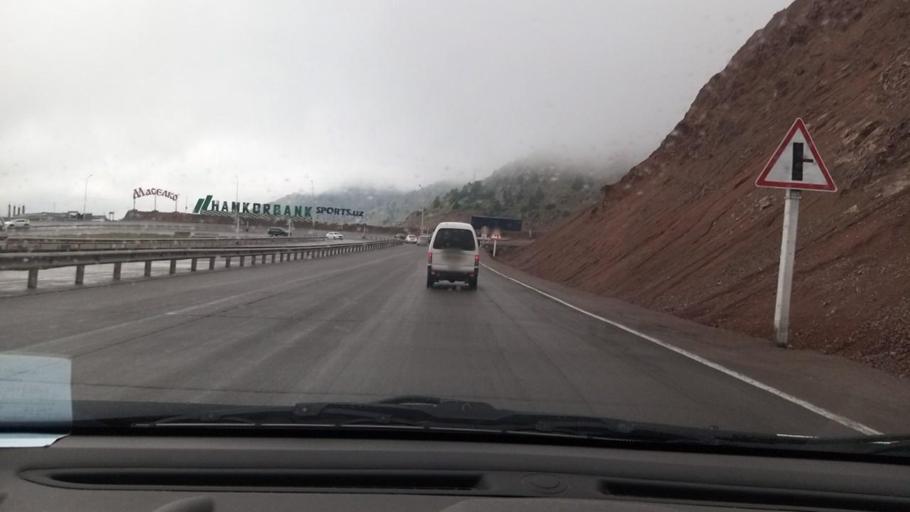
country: UZ
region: Toshkent
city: Angren
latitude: 41.1132
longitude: 70.5058
